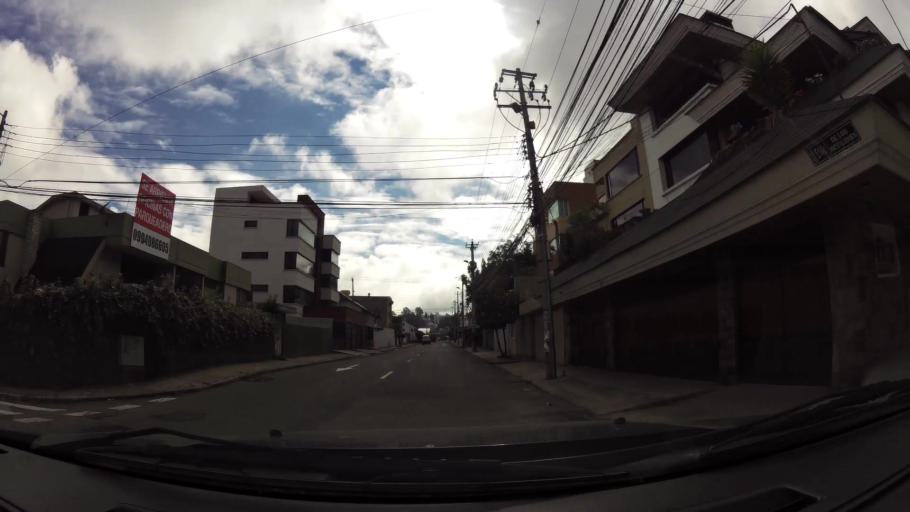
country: EC
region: Pichincha
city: Quito
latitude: -0.1669
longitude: -78.4673
